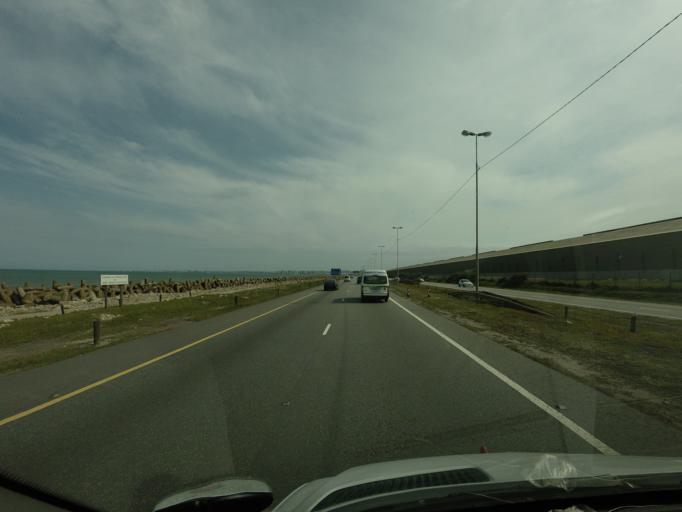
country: ZA
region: Eastern Cape
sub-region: Nelson Mandela Bay Metropolitan Municipality
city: Port Elizabeth
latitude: -33.9020
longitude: 25.6190
